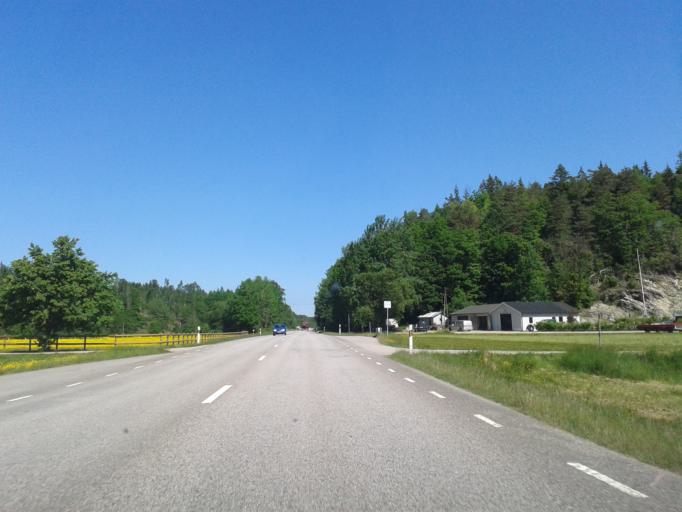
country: SE
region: Vaestra Goetaland
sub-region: Orust
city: Henan
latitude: 58.1826
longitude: 11.6945
